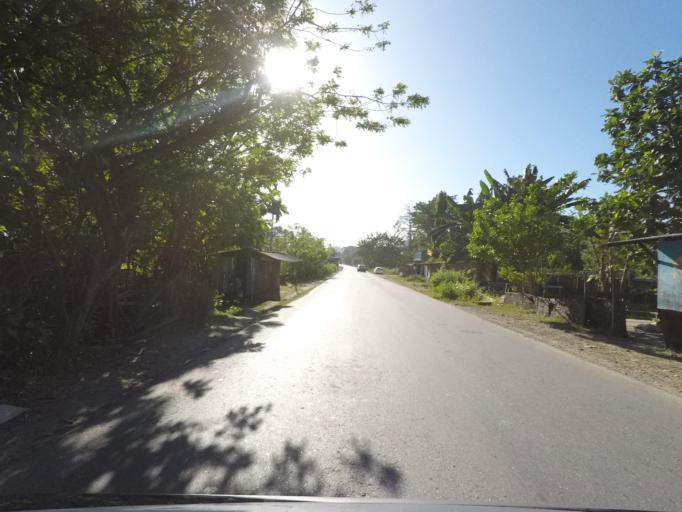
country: TL
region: Dili
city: Dili
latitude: -8.5553
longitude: 125.6546
